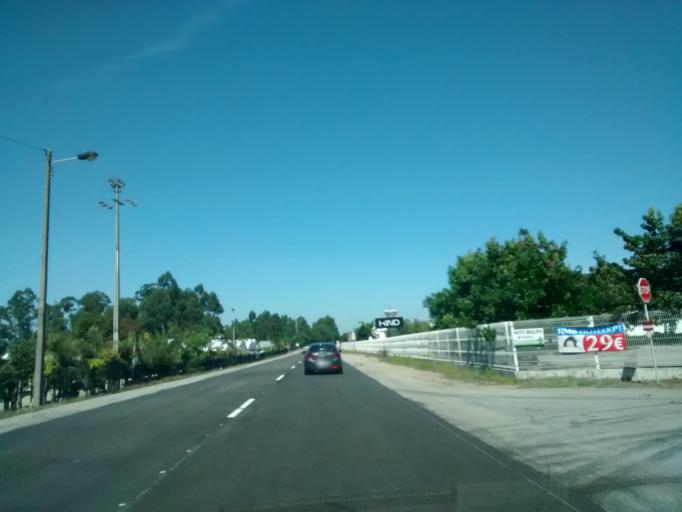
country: PT
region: Aveiro
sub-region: Oliveira do Bairro
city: Oia
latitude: 40.5381
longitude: -8.5259
